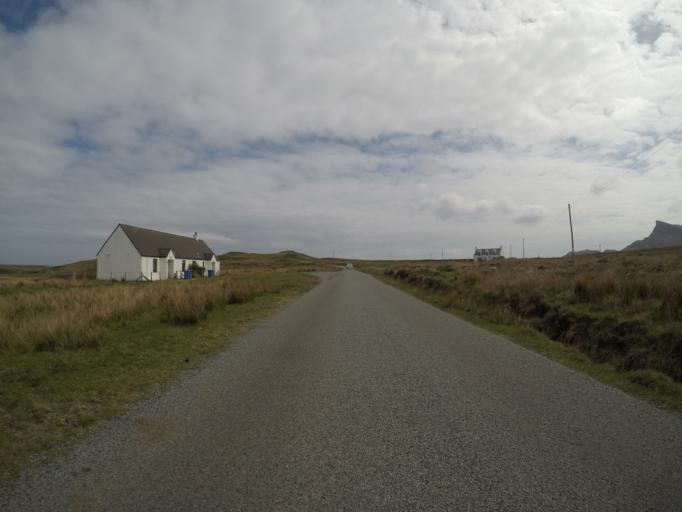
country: GB
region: Scotland
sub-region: Highland
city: Portree
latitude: 57.6814
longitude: -6.2898
